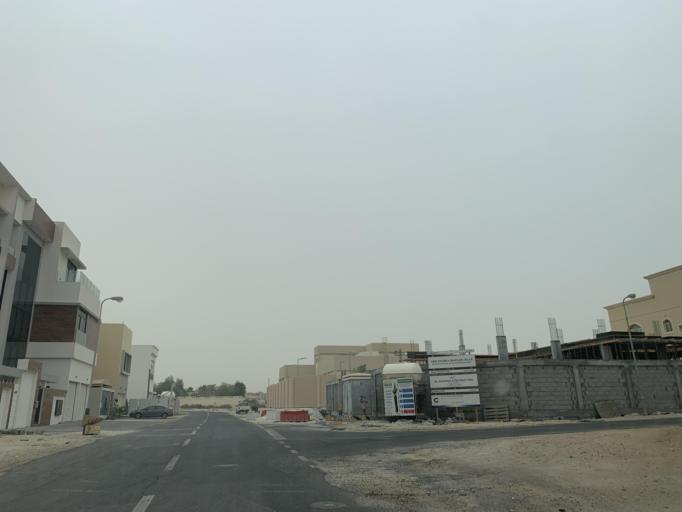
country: BH
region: Northern
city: Ar Rifa'
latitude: 26.1462
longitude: 50.5297
